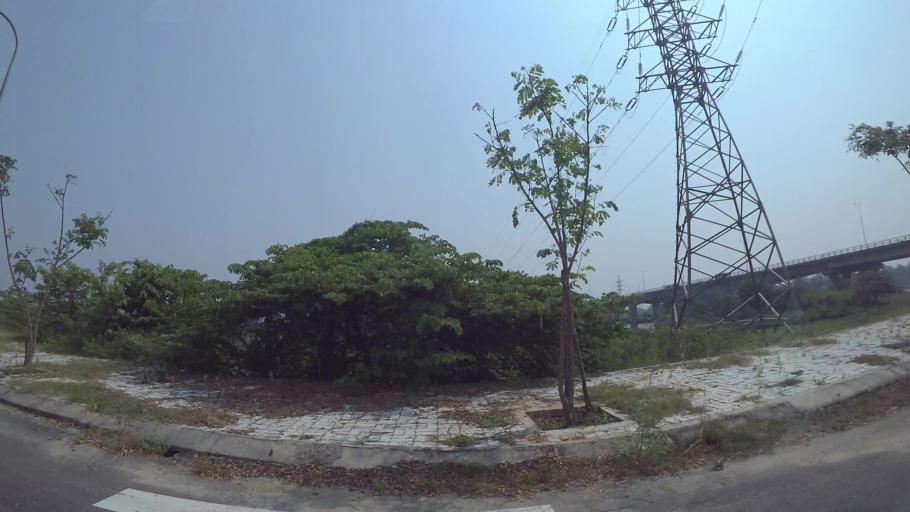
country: VN
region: Da Nang
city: Cam Le
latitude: 15.9694
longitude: 108.2157
